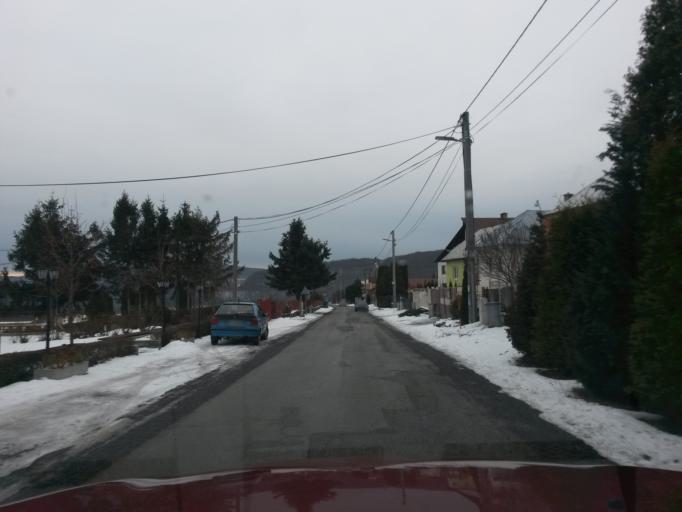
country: SK
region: Kosicky
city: Kosice
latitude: 48.7429
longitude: 21.1228
